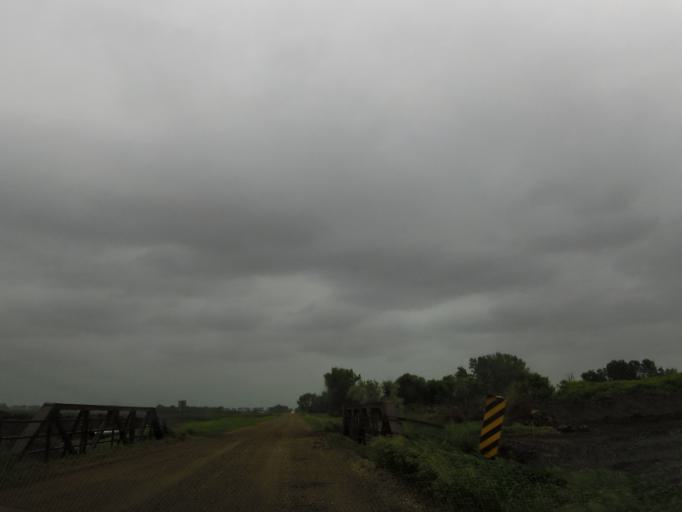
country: US
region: North Dakota
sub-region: Walsh County
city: Grafton
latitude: 48.4535
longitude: -97.4047
